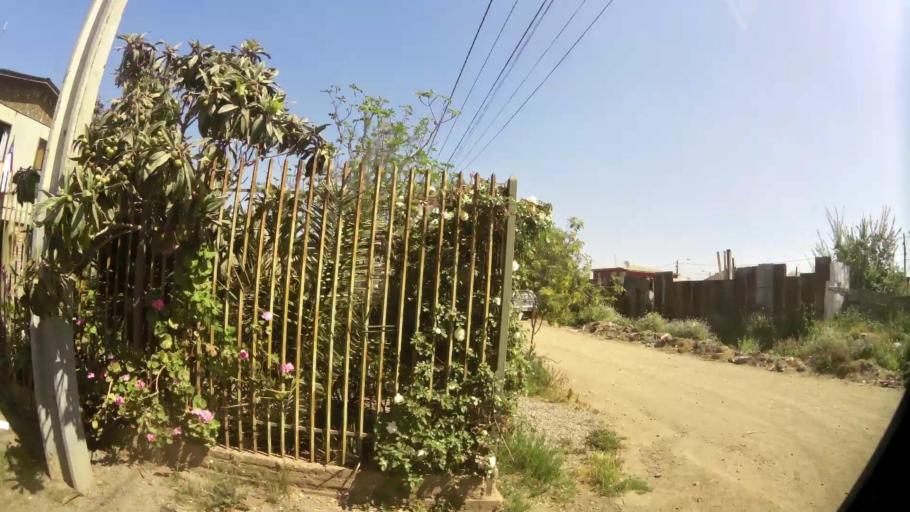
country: CL
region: Santiago Metropolitan
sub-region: Provincia de Talagante
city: Penaflor
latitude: -33.5789
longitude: -70.8054
